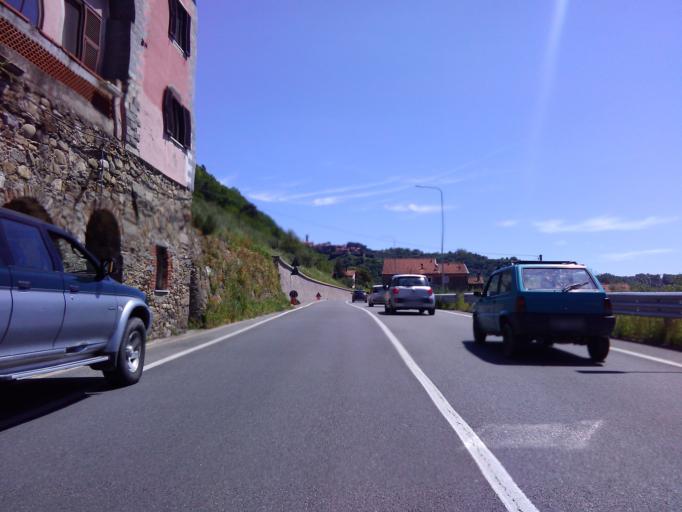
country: IT
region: Tuscany
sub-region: Provincia di Massa-Carrara
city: Albiano Magra
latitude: 44.1834
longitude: 9.9261
